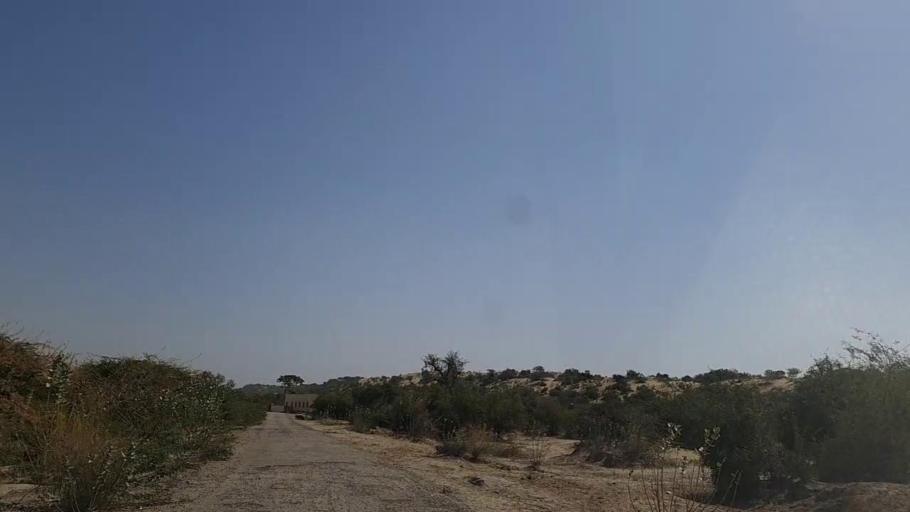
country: PK
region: Sindh
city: Mithi
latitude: 24.7032
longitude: 69.5931
